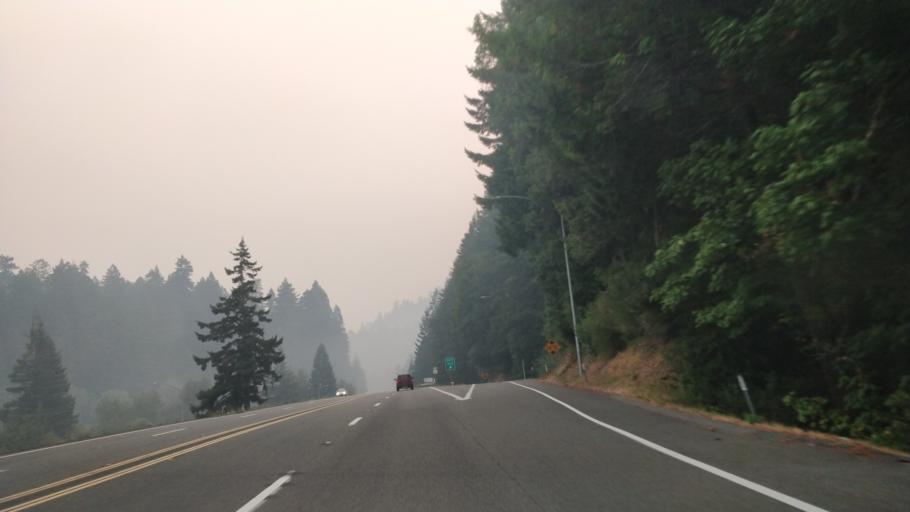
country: US
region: California
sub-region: Humboldt County
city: Rio Dell
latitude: 40.3569
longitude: -123.9232
